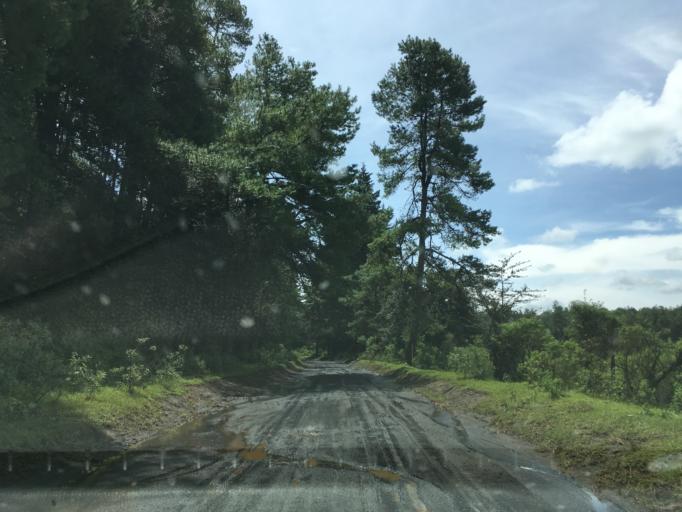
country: MX
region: Michoacan
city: Angahuan
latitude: 19.5105
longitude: -102.2143
